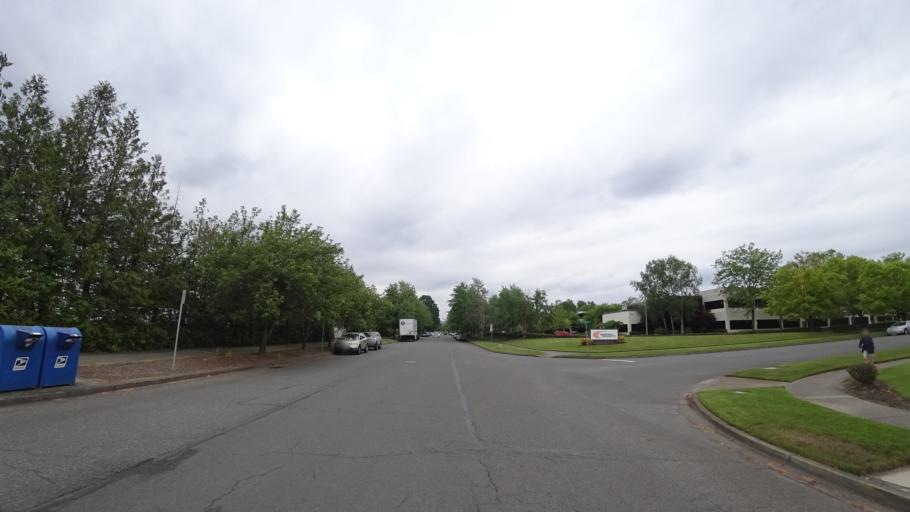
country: US
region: Oregon
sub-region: Washington County
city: Raleigh Hills
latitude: 45.4757
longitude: -122.7787
